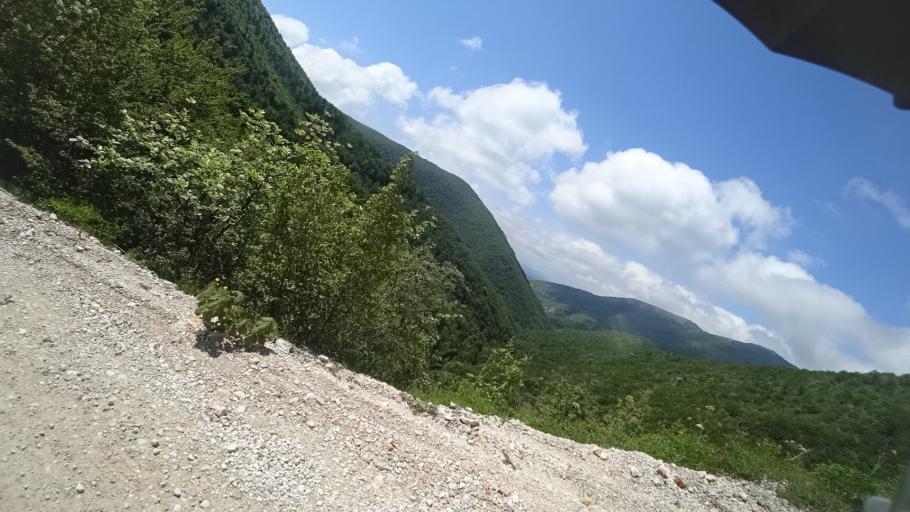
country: BA
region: Federation of Bosnia and Herzegovina
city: Orasac
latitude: 44.5743
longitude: 15.8568
